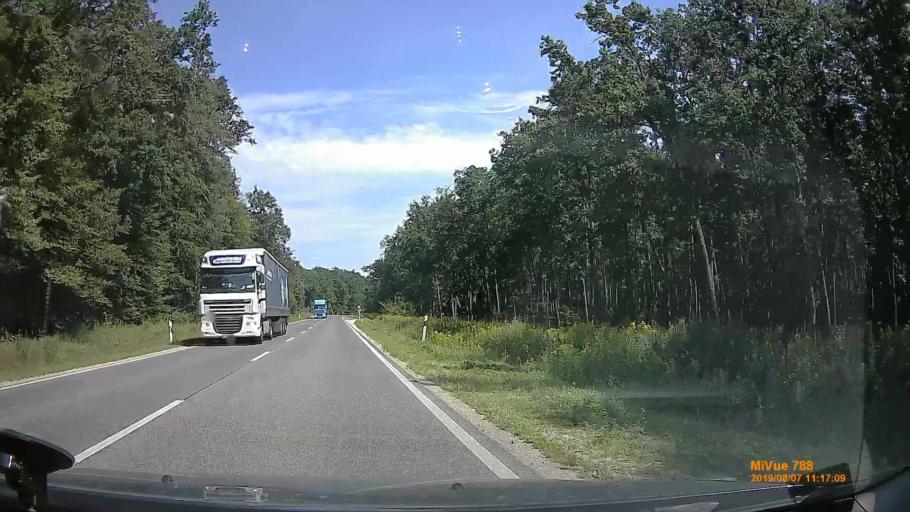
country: HU
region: Zala
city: Lenti
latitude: 46.7370
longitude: 16.5534
